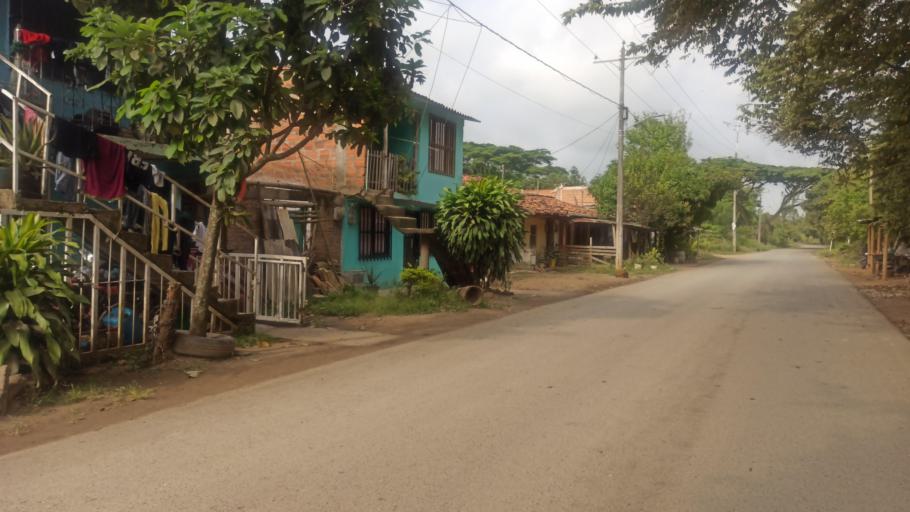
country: CO
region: Valle del Cauca
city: Jamundi
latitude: 3.2032
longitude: -76.4996
